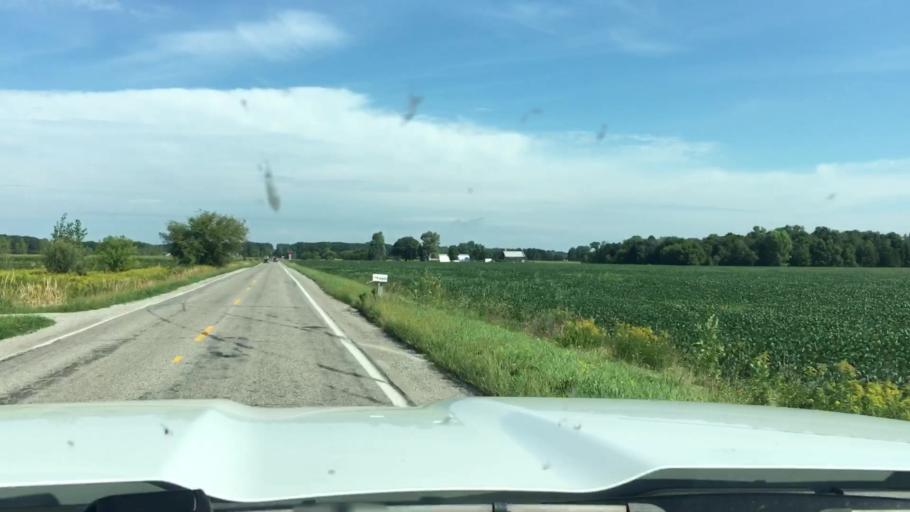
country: US
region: Michigan
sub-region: Saginaw County
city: Hemlock
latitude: 43.4446
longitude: -84.2301
